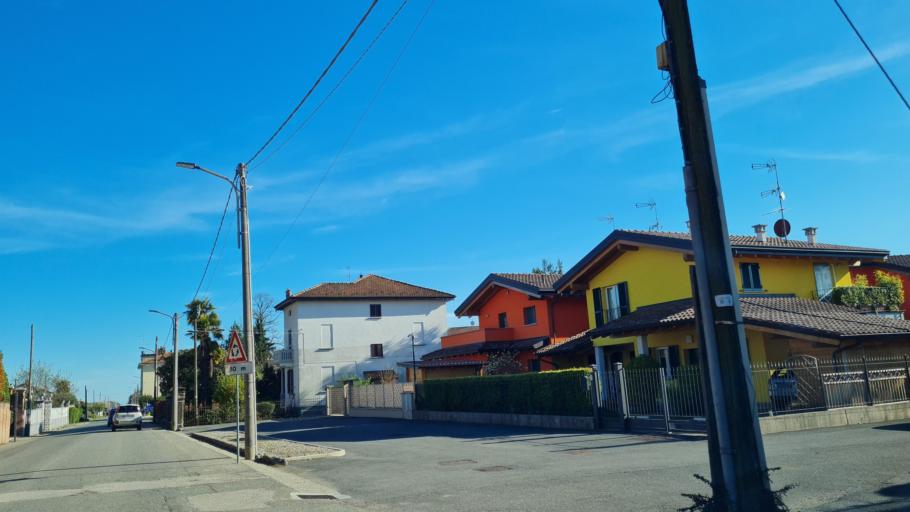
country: IT
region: Piedmont
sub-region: Provincia di Novara
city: Maggiora
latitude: 45.6888
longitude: 8.4267
